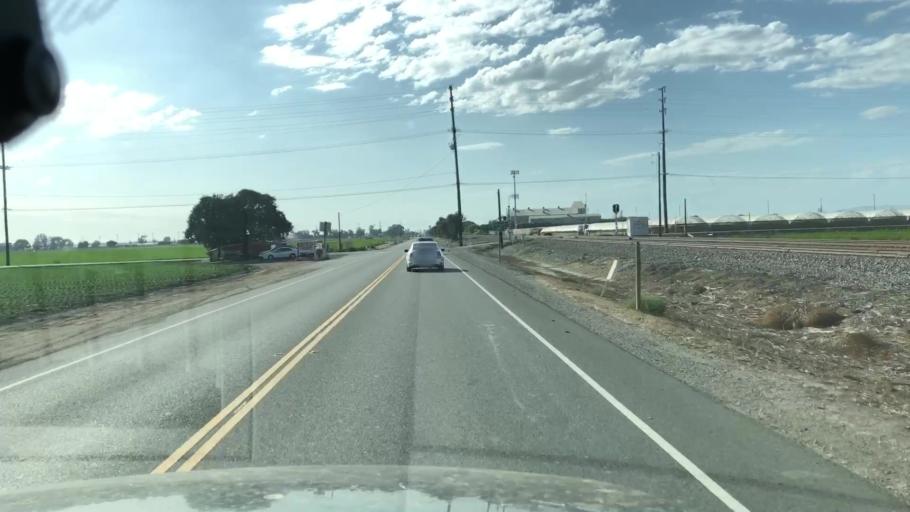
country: US
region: California
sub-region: Ventura County
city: Camarillo
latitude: 34.1966
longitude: -119.0947
